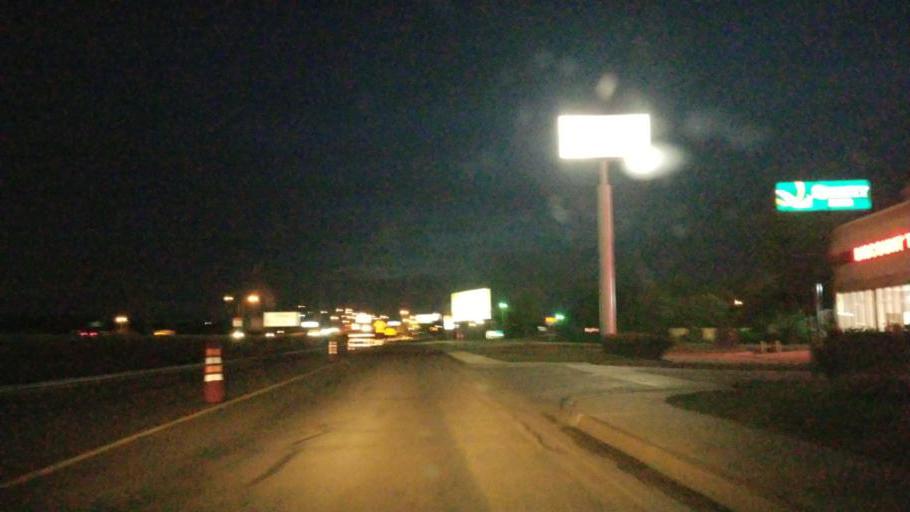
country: US
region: Texas
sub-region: Potter County
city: Amarillo
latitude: 35.1929
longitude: -101.8203
